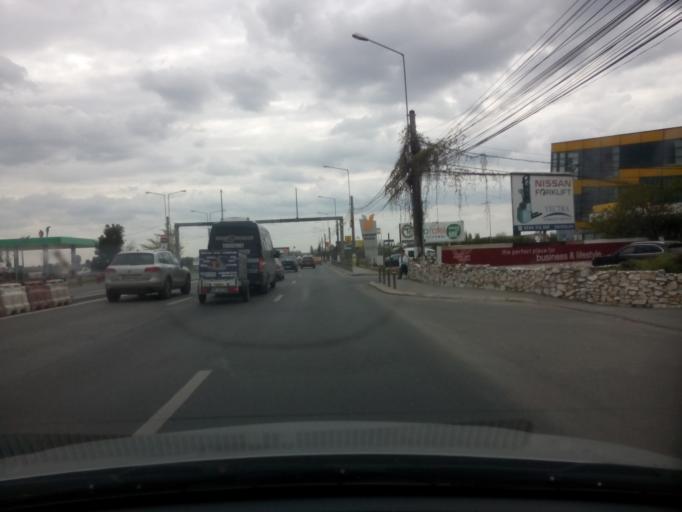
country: RO
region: Ilfov
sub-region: Comuna Otopeni
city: Otopeni
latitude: 44.5680
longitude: 26.0697
